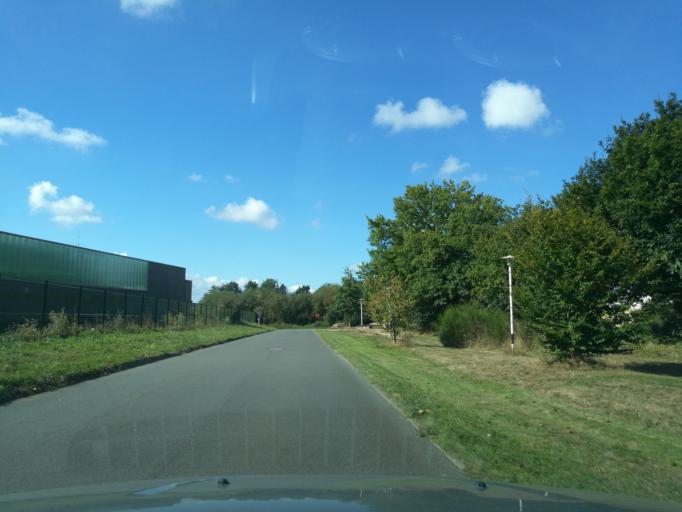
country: FR
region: Brittany
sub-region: Departement d'Ille-et-Vilaine
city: Pleumeleuc
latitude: 48.1852
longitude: -1.9283
